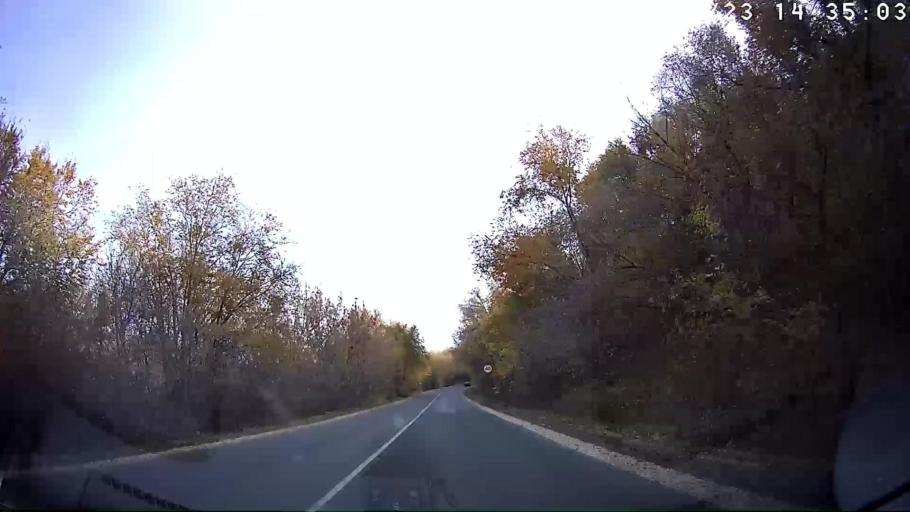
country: RU
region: Volgograd
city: Krasnoslobodsk
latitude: 48.5090
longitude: 44.5275
